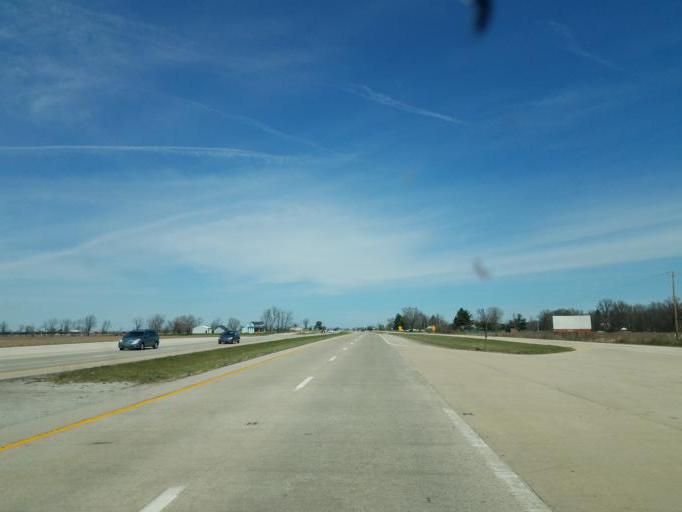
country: US
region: Ohio
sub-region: Delaware County
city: Delaware
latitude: 40.3846
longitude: -83.0738
